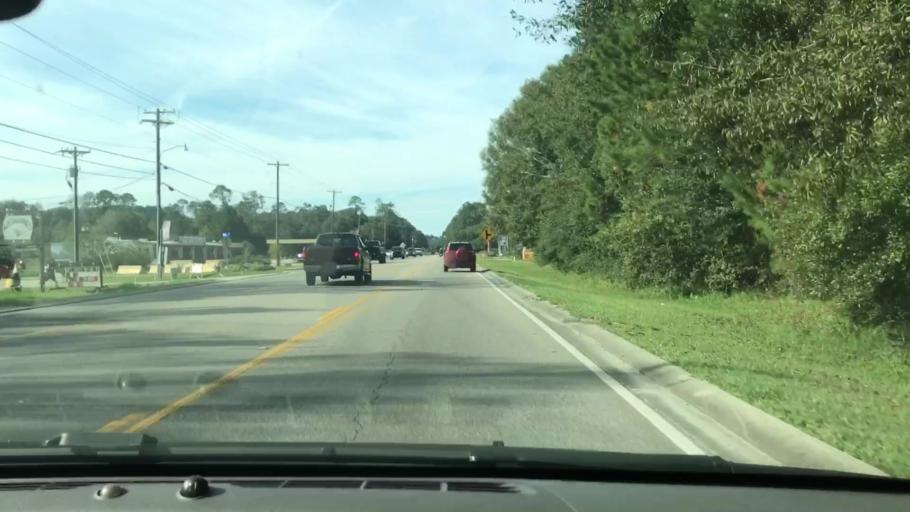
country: US
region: Louisiana
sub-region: Saint Tammany Parish
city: Pearl River
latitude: 30.3653
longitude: -89.7572
